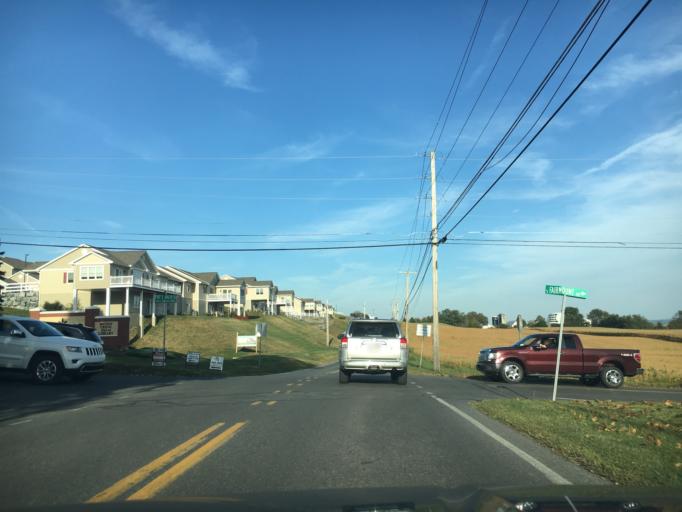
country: US
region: Pennsylvania
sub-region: Lancaster County
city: Ephrata
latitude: 40.1314
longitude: -76.1481
